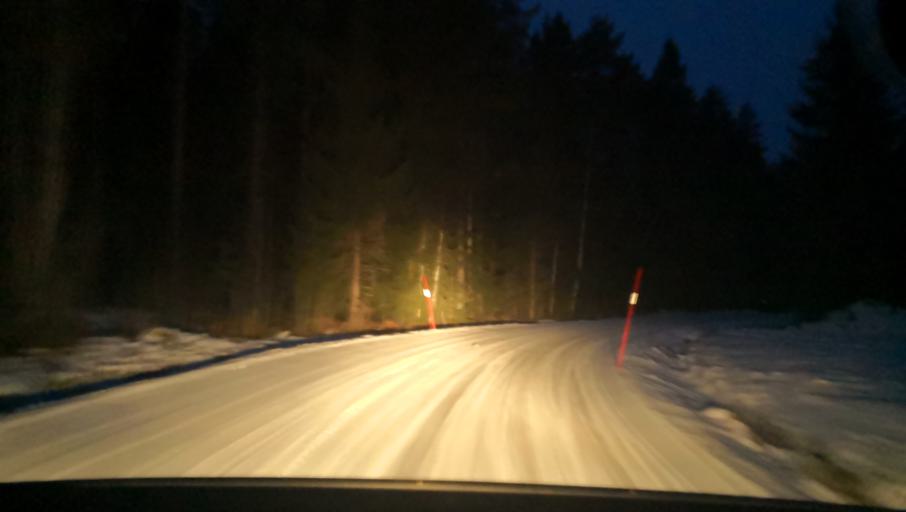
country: SE
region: Uppsala
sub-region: Heby Kommun
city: Tarnsjo
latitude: 60.2584
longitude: 16.7740
